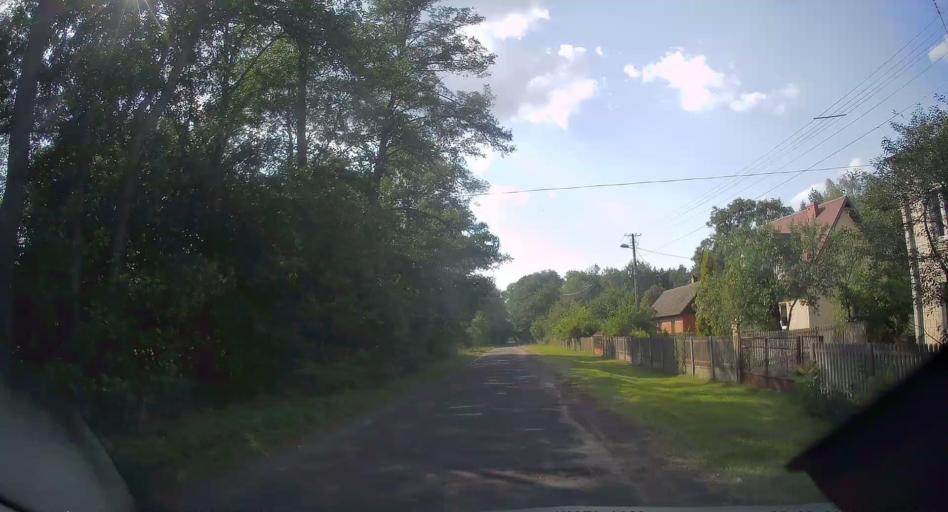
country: PL
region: Swietokrzyskie
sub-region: Powiat konecki
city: Ruda Maleniecka
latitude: 51.1295
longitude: 20.2497
